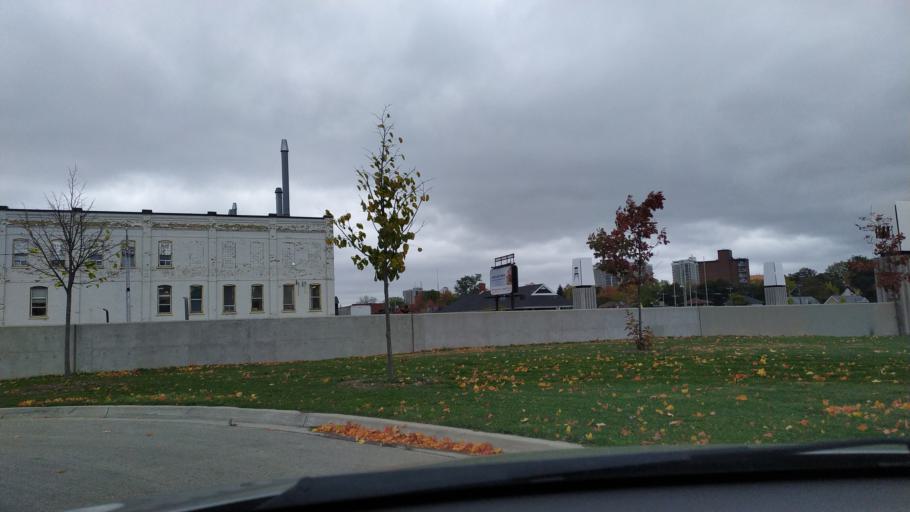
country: CA
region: Ontario
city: Waterloo
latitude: 43.4557
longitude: -80.4950
